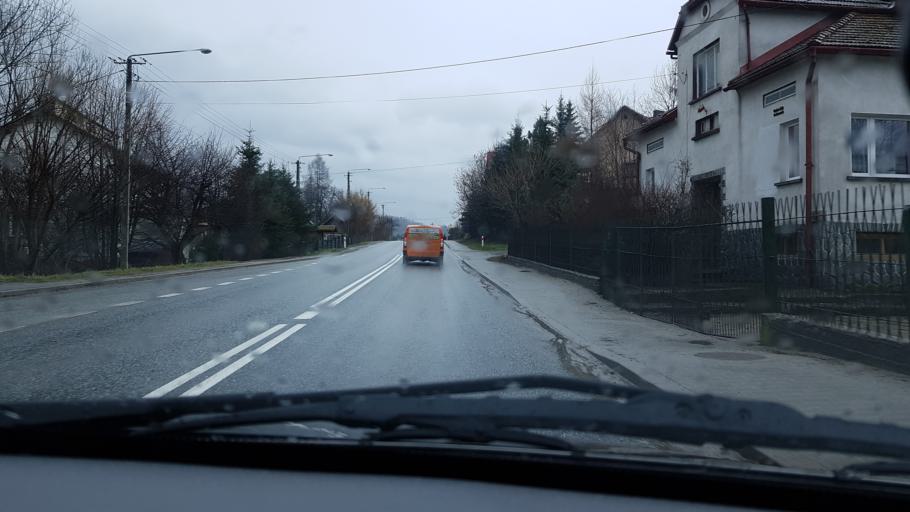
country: PL
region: Lesser Poland Voivodeship
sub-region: Powiat suski
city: Osielec
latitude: 49.6754
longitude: 19.7578
